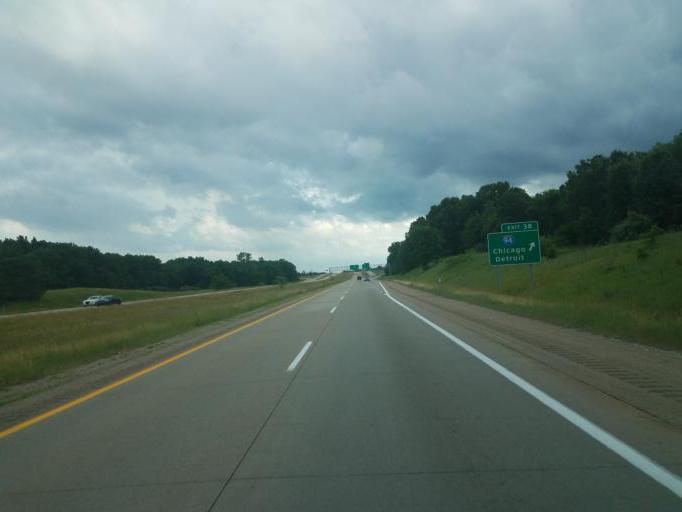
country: US
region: Michigan
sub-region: Calhoun County
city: Marshall
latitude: 42.3070
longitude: -84.9954
